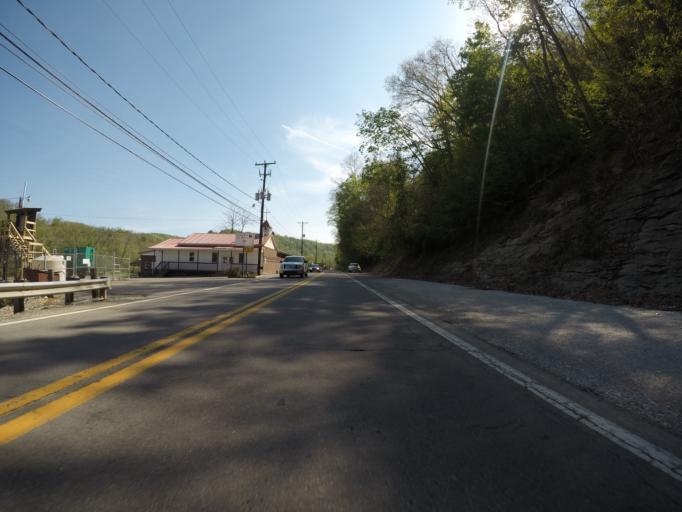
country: US
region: West Virginia
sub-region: Kanawha County
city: Clendenin
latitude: 38.4714
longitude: -81.3999
